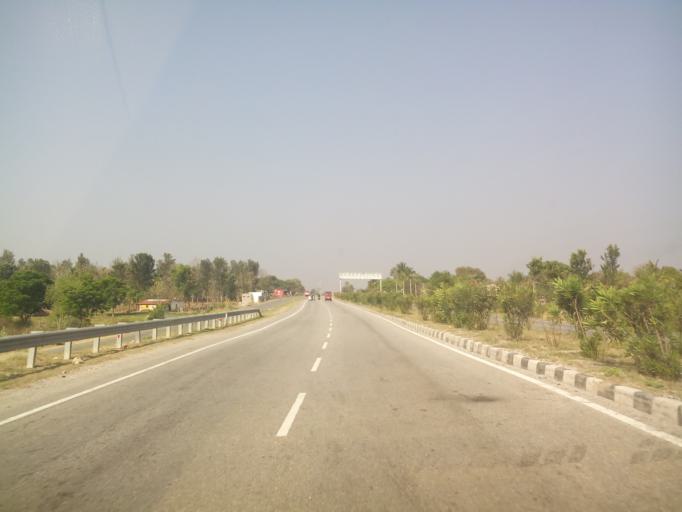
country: IN
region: Karnataka
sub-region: Tumkur
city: Kunigal
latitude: 13.0028
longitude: 76.9515
